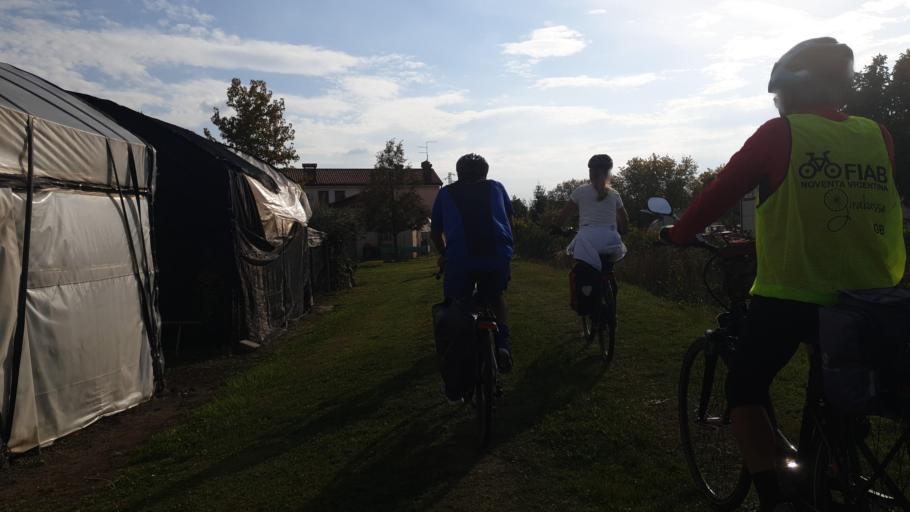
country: IT
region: Veneto
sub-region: Provincia di Vicenza
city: Poiana Maggiore
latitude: 45.2779
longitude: 11.4882
